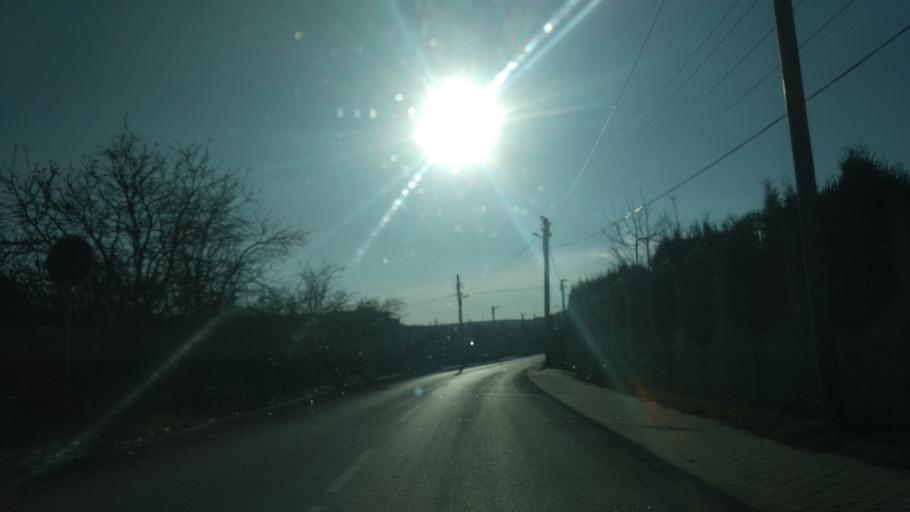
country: XK
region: Pristina
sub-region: Komuna e Prishtines
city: Pristina
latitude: 42.7139
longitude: 21.1638
